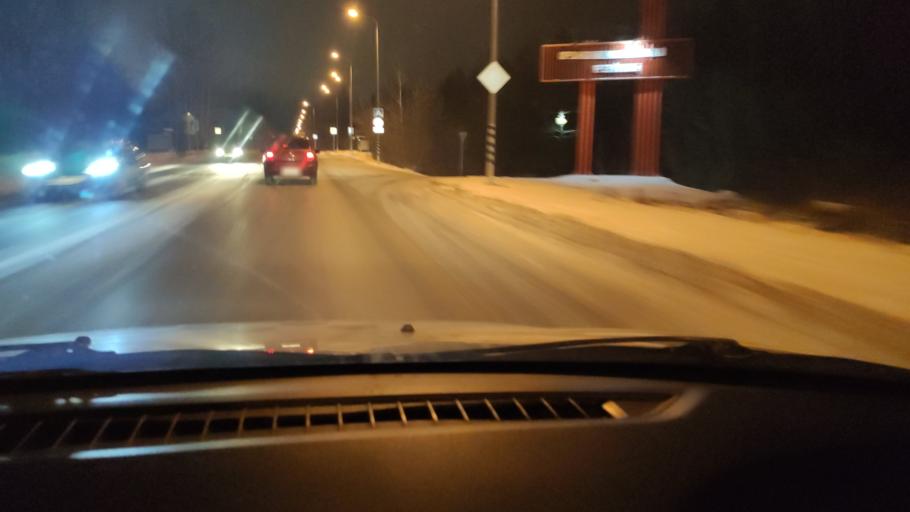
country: RU
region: Perm
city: Perm
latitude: 58.0806
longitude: 56.3088
